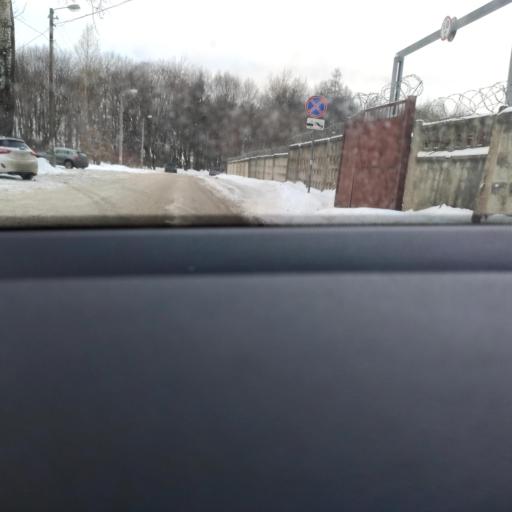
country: RU
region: Moskovskaya
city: Novopodrezkovo
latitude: 55.9842
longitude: 37.4046
